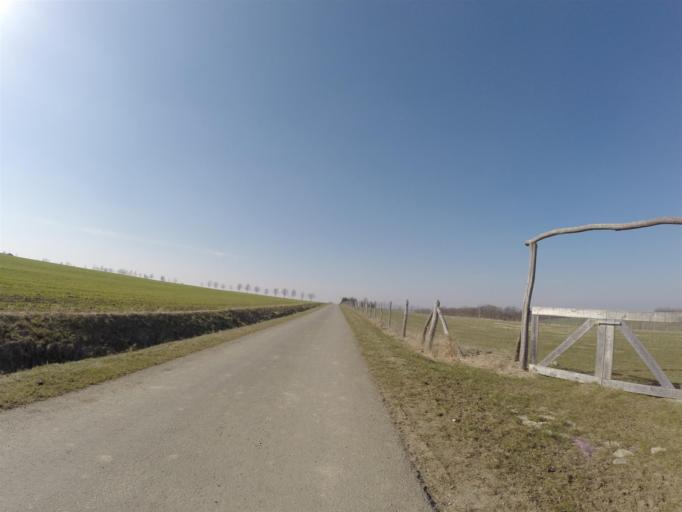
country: DE
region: Thuringia
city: Kleinschwabhausen
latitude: 50.9308
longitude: 11.4567
